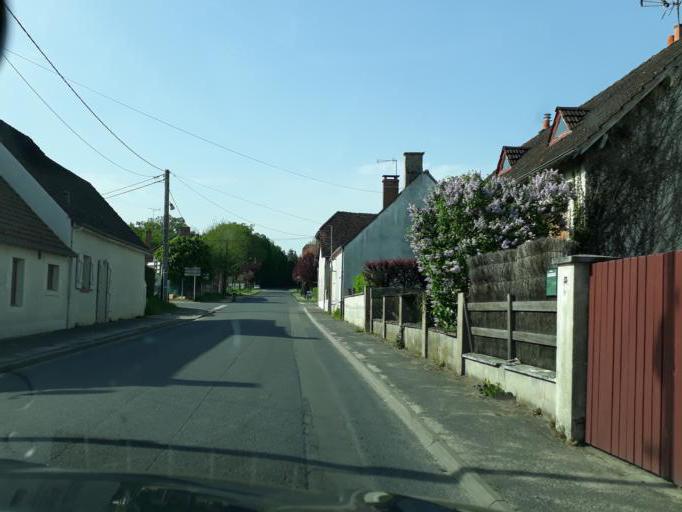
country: FR
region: Centre
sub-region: Departement du Loir-et-Cher
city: Dhuizon
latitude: 47.6593
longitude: 1.6716
